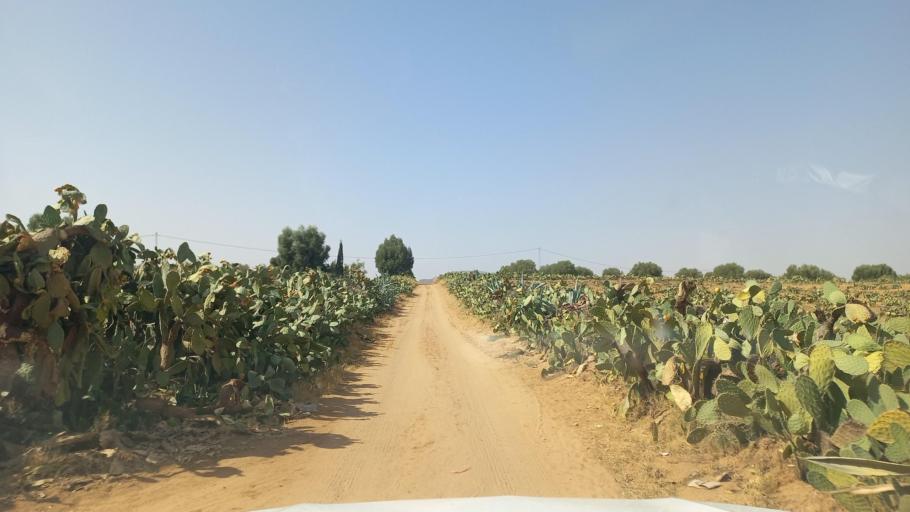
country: TN
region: Al Qasrayn
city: Kasserine
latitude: 35.2331
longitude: 9.0527
